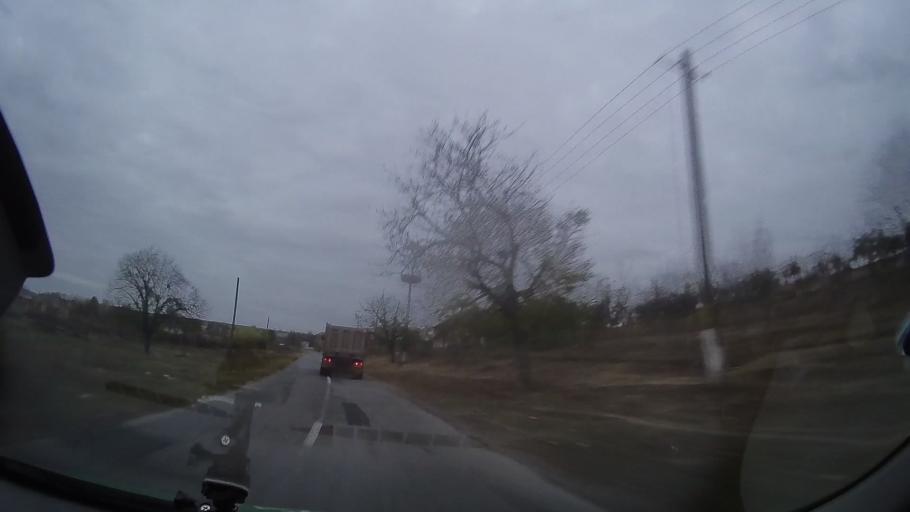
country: RO
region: Tulcea
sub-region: Comuna Mihai Bravu
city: Mihai Bravu
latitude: 44.9568
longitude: 28.6501
